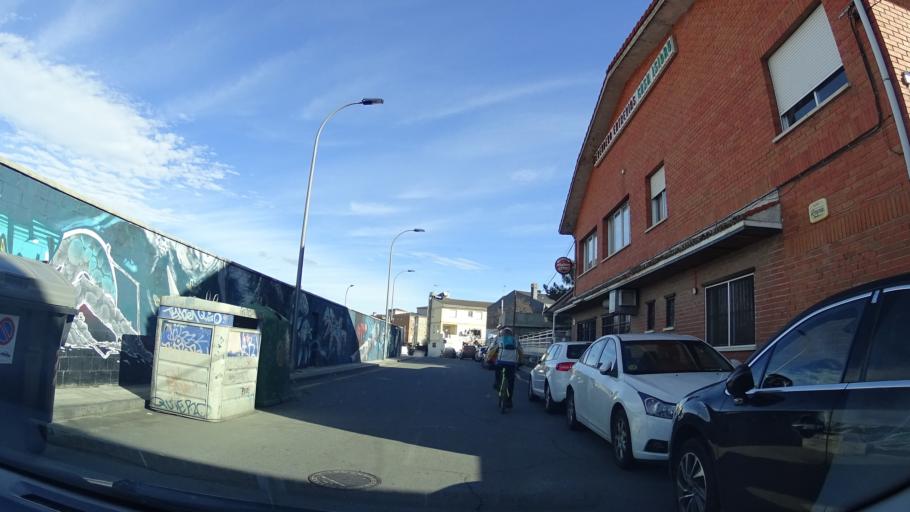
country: ES
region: Madrid
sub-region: Provincia de Madrid
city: Collado-Villalba
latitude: 40.6262
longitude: -4.0143
